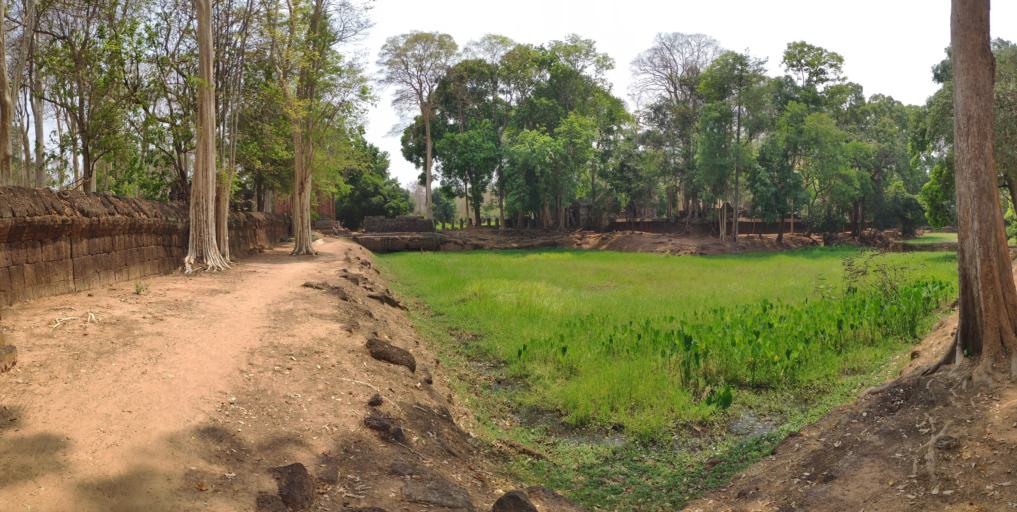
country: KH
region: Preah Vihear
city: Tbeng Meanchey
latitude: 13.7844
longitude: 104.5397
